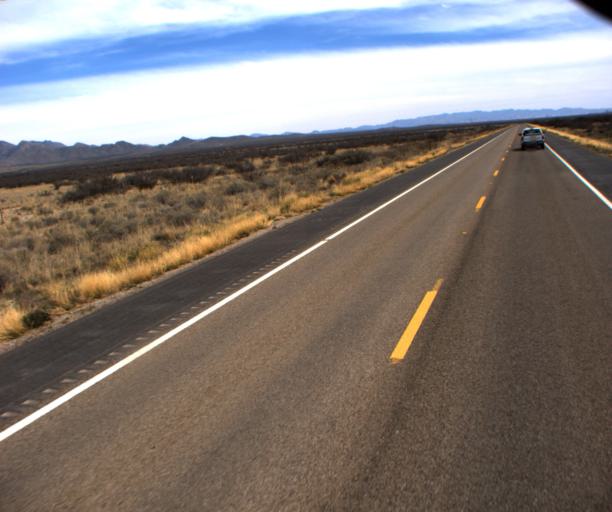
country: US
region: Arizona
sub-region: Cochise County
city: Willcox
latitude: 32.2039
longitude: -109.7701
